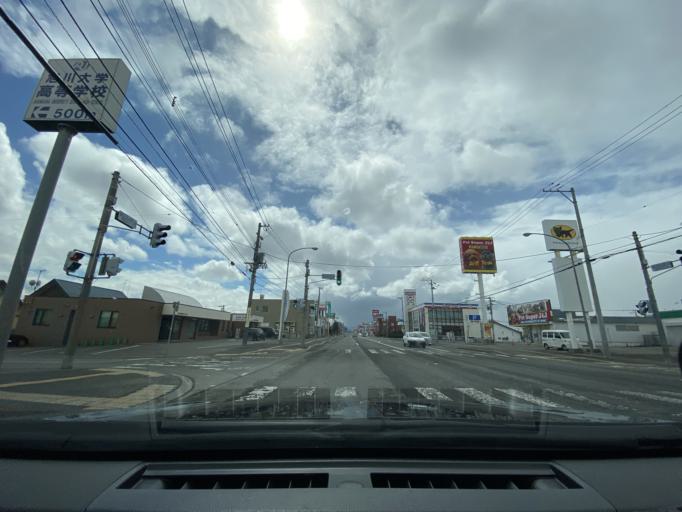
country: JP
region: Hokkaido
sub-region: Asahikawa-shi
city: Asahikawa
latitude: 43.8076
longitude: 142.4294
